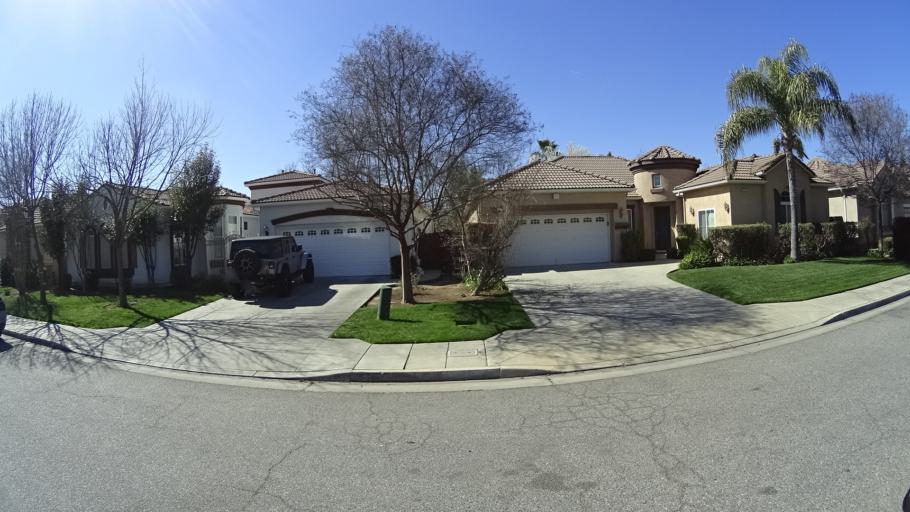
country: US
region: California
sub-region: Fresno County
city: Clovis
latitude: 36.8574
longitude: -119.7315
